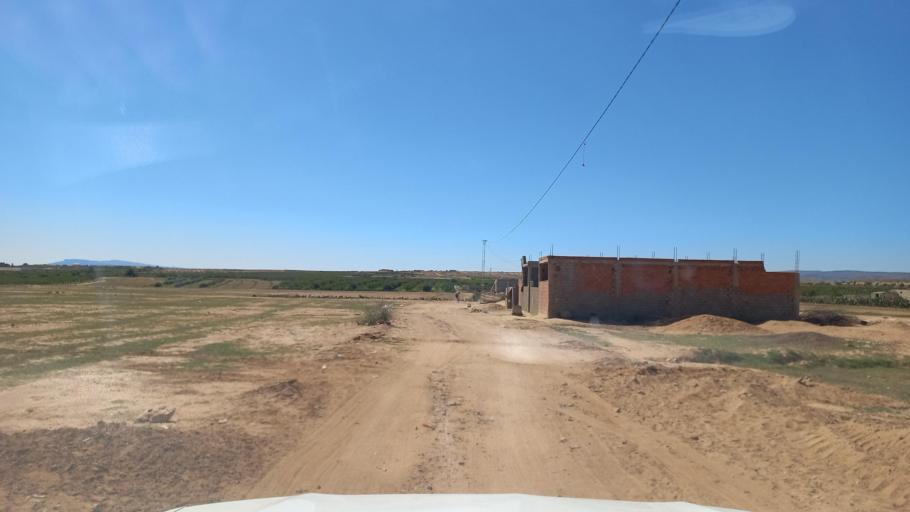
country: TN
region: Al Qasrayn
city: Sbiba
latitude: 35.3595
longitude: 9.0886
